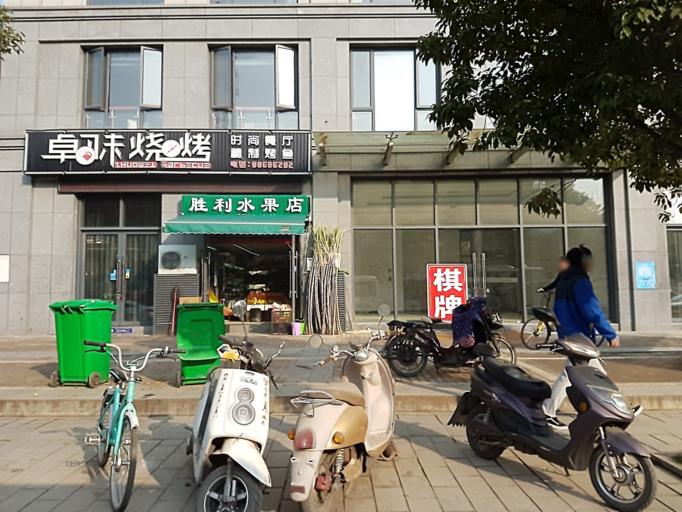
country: CN
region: Zhejiang Sheng
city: Jiangcun
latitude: 30.2941
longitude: 120.0380
